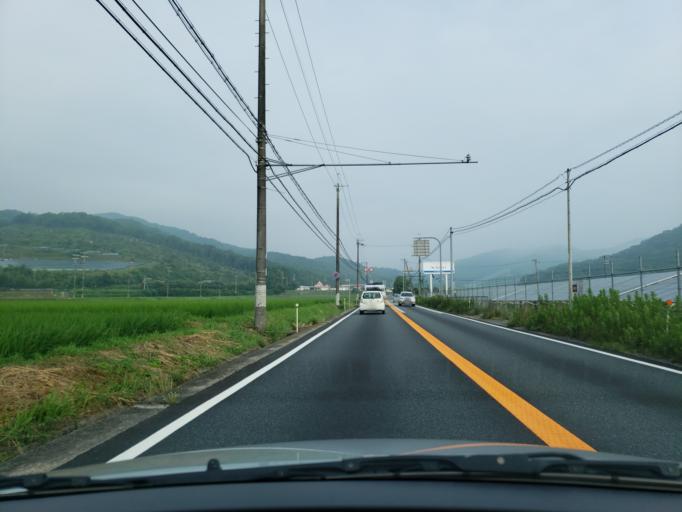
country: JP
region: Hyogo
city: Kariya
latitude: 34.8345
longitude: 134.3487
